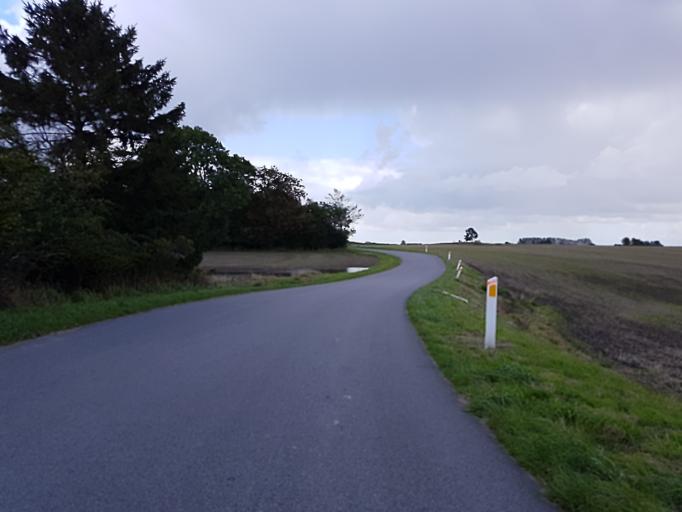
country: DK
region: Zealand
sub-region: Roskilde Kommune
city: Gundsomagle
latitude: 55.7219
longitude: 12.1633
